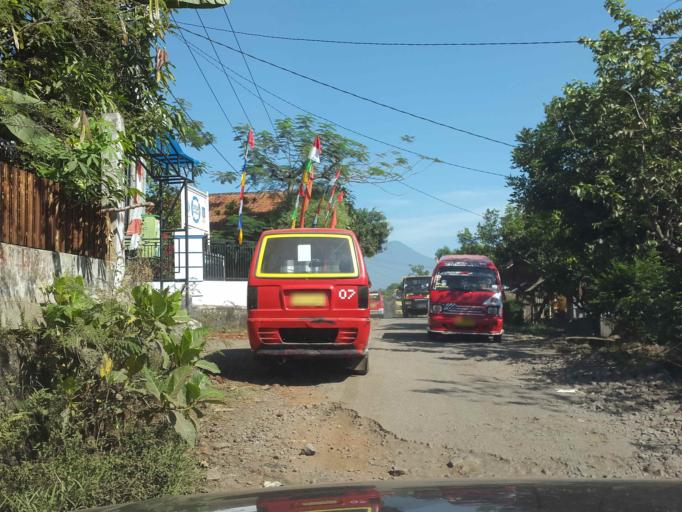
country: ID
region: West Java
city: Ciranjang-hilir
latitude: -6.8597
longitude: 107.1947
